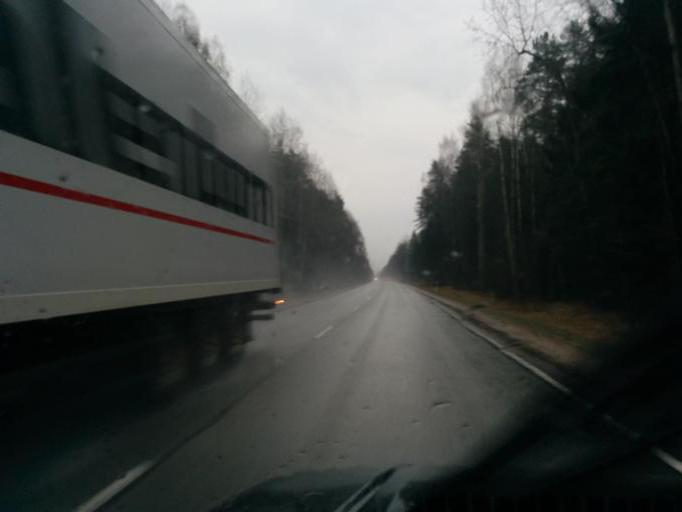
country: LV
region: Kekava
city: Balozi
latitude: 56.8224
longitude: 24.0806
